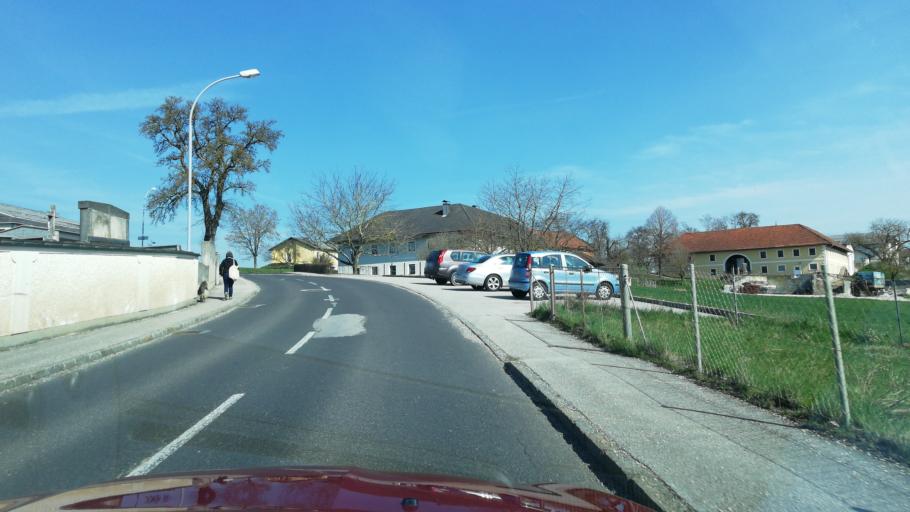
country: AT
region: Upper Austria
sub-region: Politischer Bezirk Kirchdorf an der Krems
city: Kremsmunster
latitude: 48.0996
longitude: 14.1106
